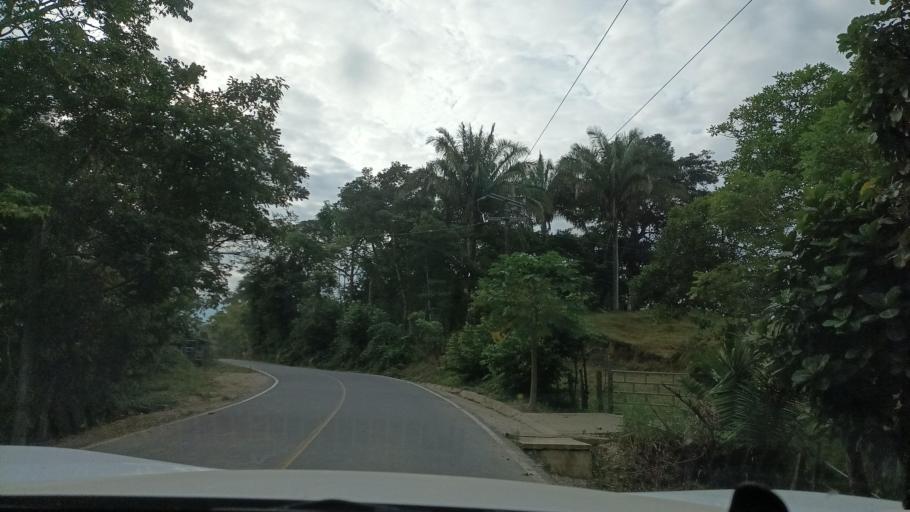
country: MX
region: Veracruz
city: Hidalgotitlan
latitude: 17.7493
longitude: -94.4958
